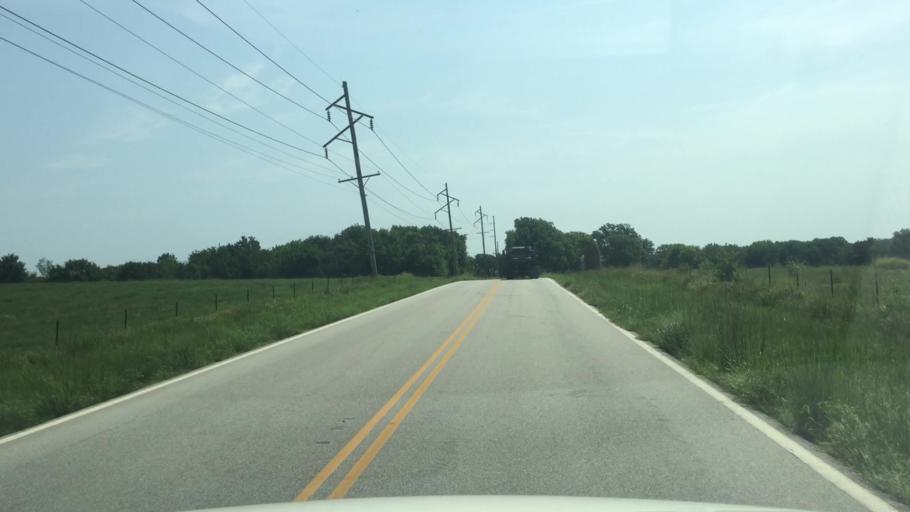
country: US
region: Kansas
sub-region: Montgomery County
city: Cherryvale
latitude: 37.2080
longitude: -95.5609
